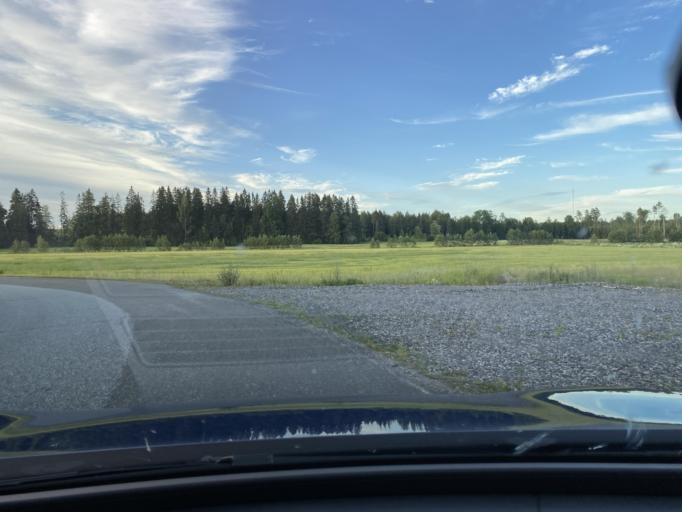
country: FI
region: Pirkanmaa
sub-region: Lounais-Pirkanmaa
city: Punkalaidun
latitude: 61.0408
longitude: 22.9998
